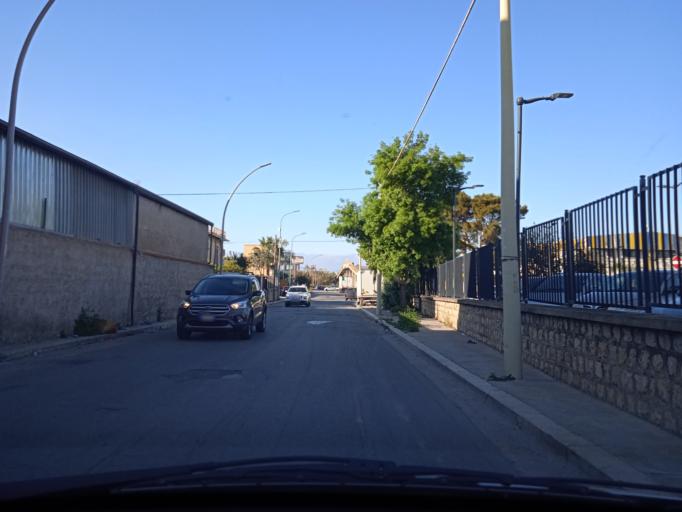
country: IT
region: Sicily
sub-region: Palermo
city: Villabate
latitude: 38.0848
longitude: 13.4497
